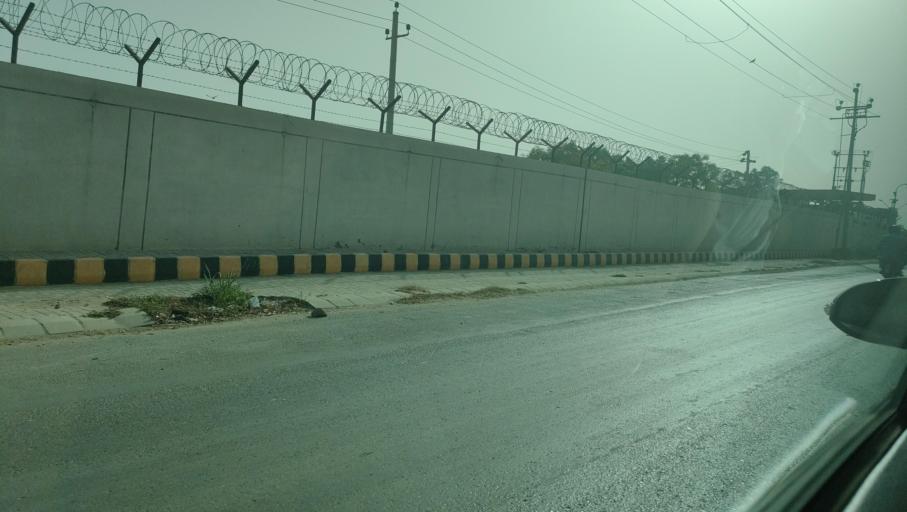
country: PK
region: Sindh
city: Malir Cantonment
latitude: 24.9230
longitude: 67.1829
